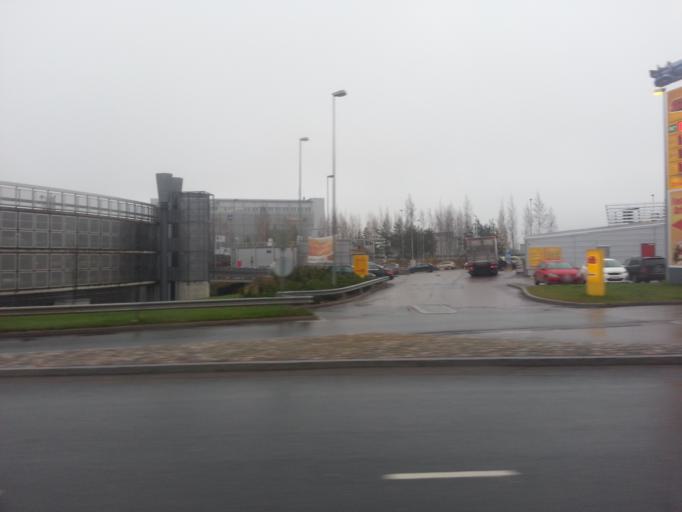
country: FI
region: Uusimaa
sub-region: Helsinki
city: Vantaa
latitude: 60.3132
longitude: 24.9699
